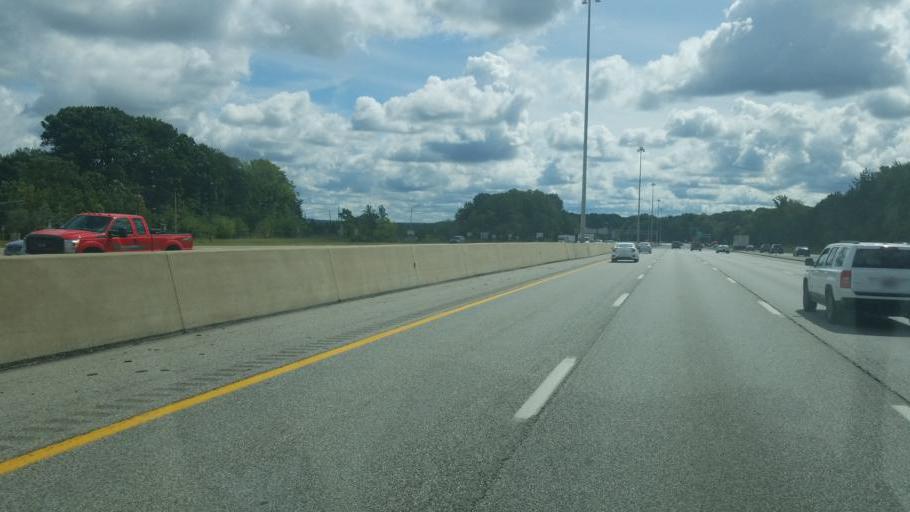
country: US
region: Ohio
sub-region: Cuyahoga County
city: Brooklyn Heights
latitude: 41.4168
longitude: -81.6772
